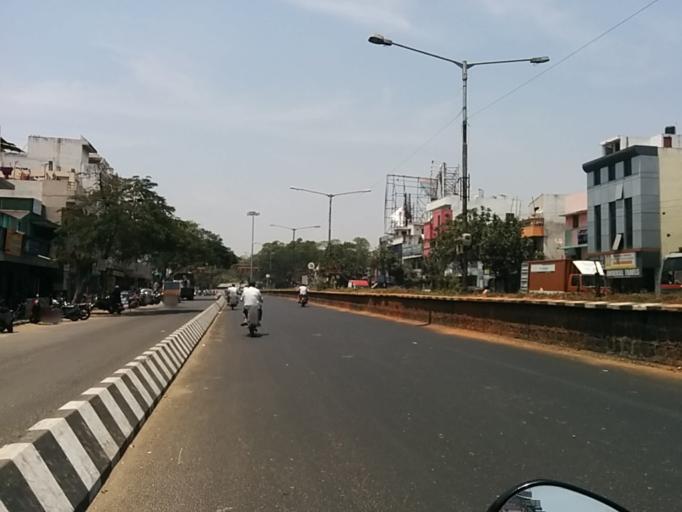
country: IN
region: Pondicherry
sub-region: Puducherry
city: Puducherry
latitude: 11.9324
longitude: 79.8135
